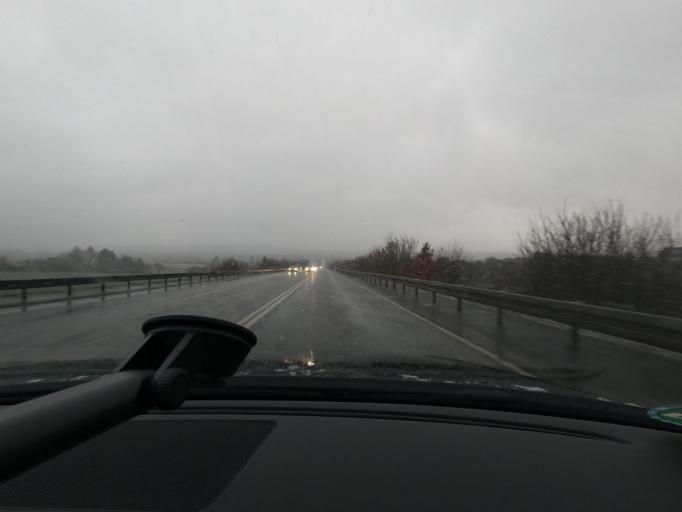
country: DE
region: Thuringia
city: Dingelstadt
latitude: 51.3206
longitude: 10.3288
